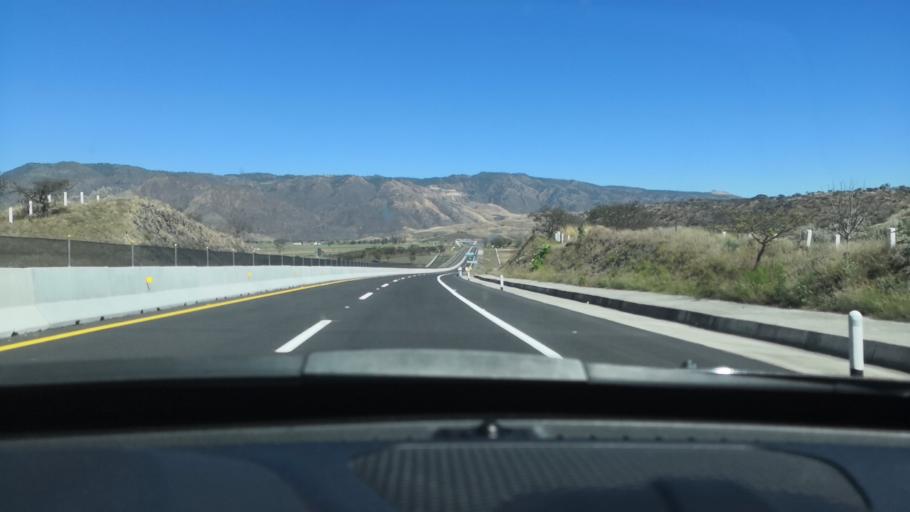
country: MX
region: Nayarit
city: Jala
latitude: 21.0747
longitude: -104.4514
